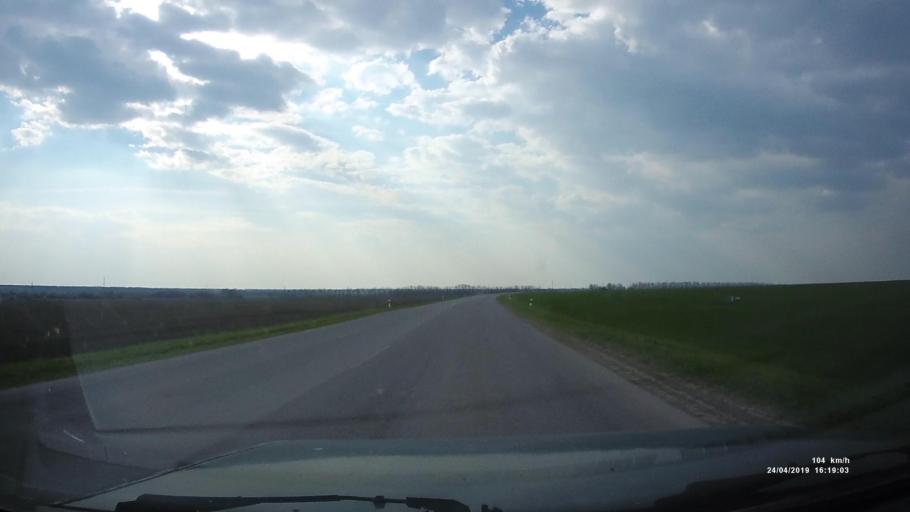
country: RU
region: Rostov
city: Sovetskoye
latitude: 46.7781
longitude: 42.1031
